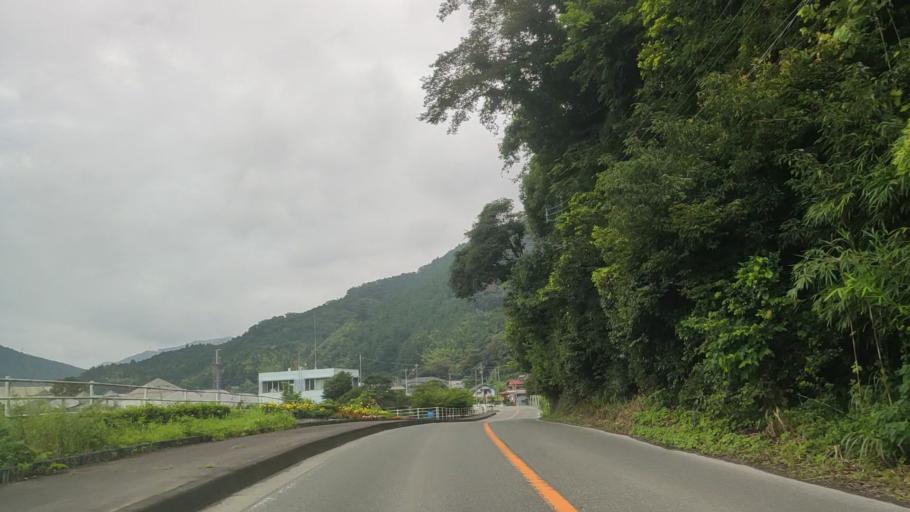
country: JP
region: Shizuoka
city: Fujinomiya
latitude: 35.2069
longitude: 138.5541
